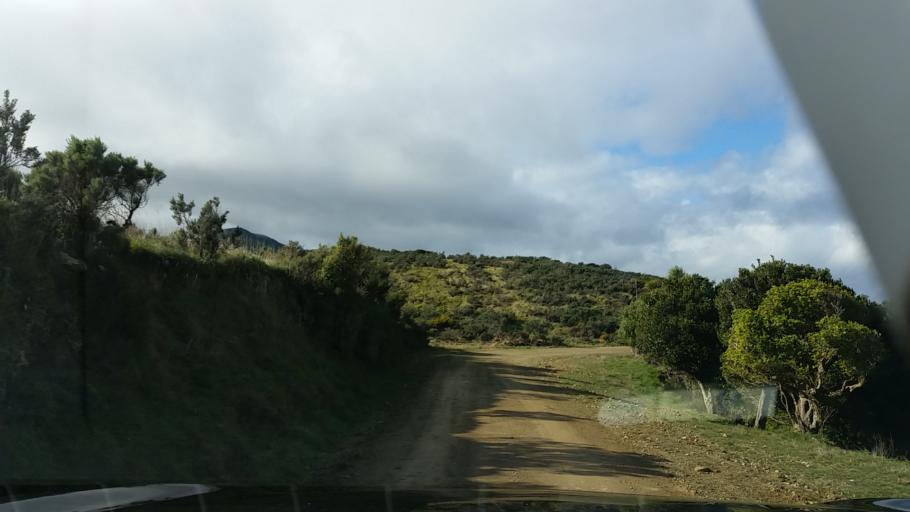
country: NZ
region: Marlborough
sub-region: Marlborough District
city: Picton
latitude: -40.9673
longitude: 173.8925
